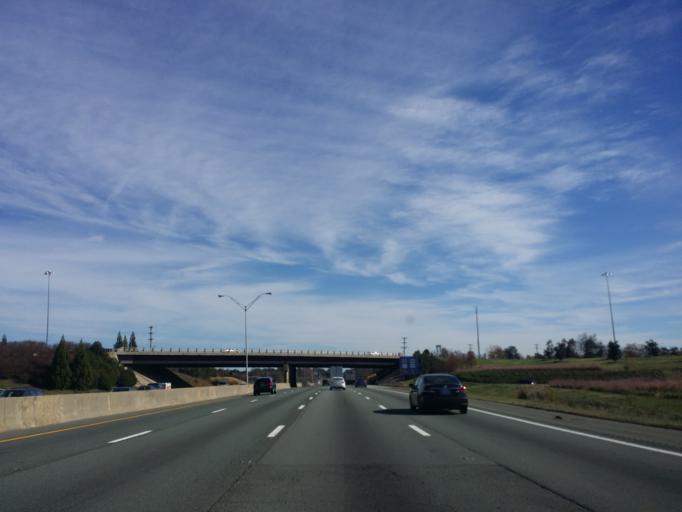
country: US
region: North Carolina
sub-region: Alamance County
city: Elon
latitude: 36.0651
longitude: -79.5179
